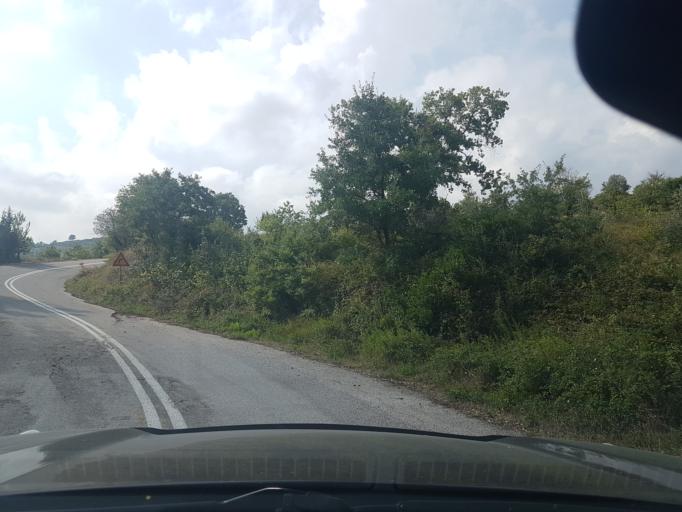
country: GR
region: Central Greece
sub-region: Nomos Evvoias
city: Yimnon
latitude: 38.5368
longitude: 23.9692
